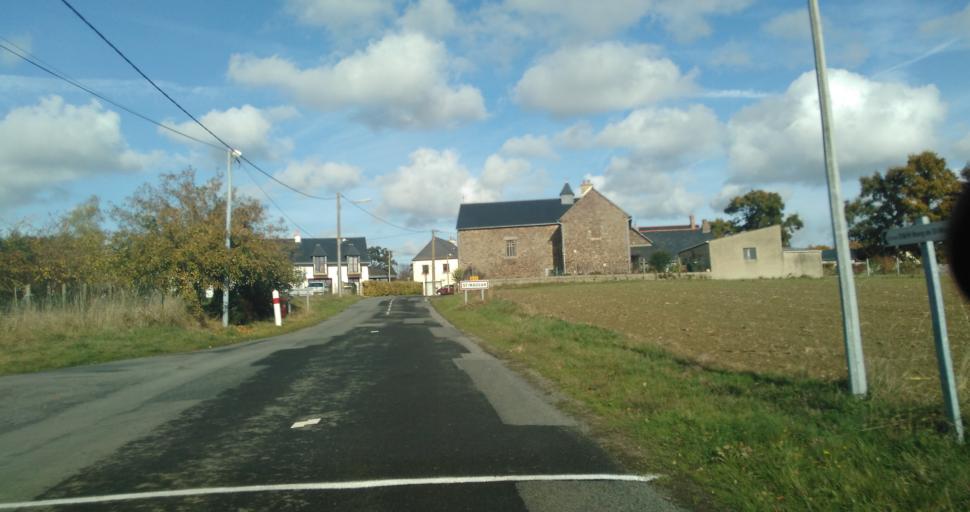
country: FR
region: Brittany
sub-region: Departement d'Ille-et-Vilaine
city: Boisgervilly
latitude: 48.1293
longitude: -2.0841
